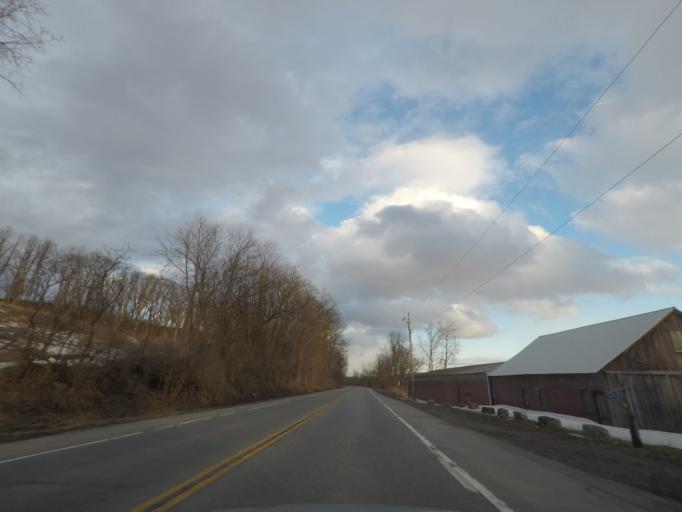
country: US
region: New York
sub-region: Montgomery County
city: Saint Johnsville
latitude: 43.0087
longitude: -74.7602
